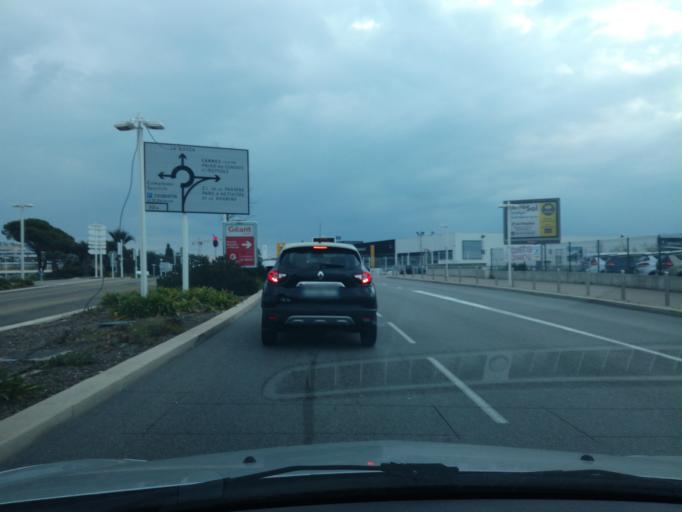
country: FR
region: Provence-Alpes-Cote d'Azur
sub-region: Departement des Alpes-Maritimes
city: Mandelieu-la-Napoule
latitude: 43.5501
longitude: 6.9613
